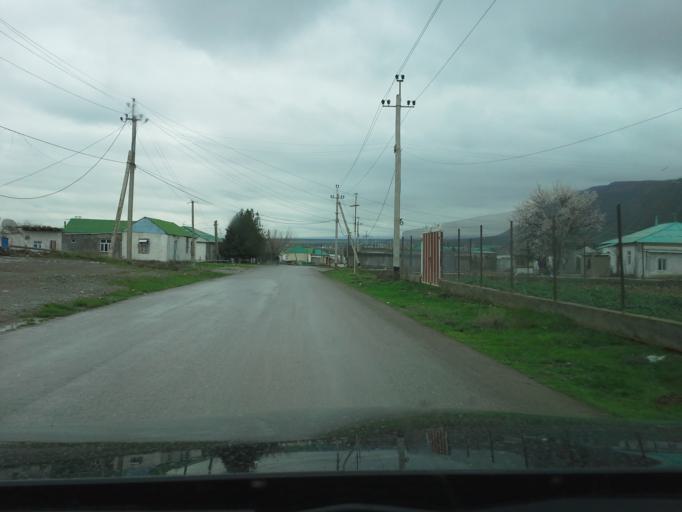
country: TM
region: Ahal
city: Abadan
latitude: 37.9496
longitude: 58.2069
